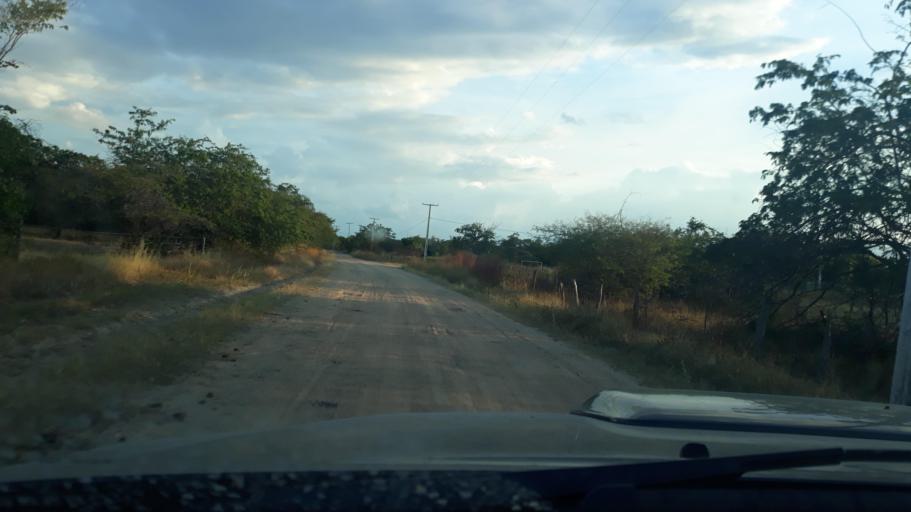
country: BR
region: Bahia
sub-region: Riacho De Santana
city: Riacho de Santana
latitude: -13.8734
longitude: -43.0200
